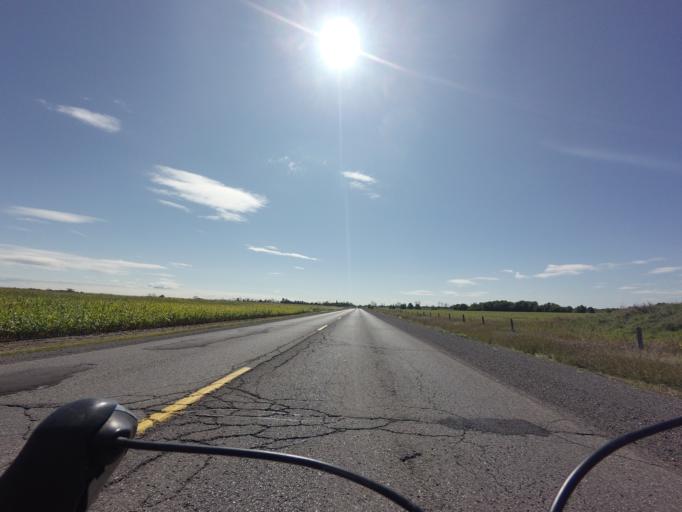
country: CA
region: Ontario
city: Bells Corners
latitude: 45.2196
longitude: -75.8310
